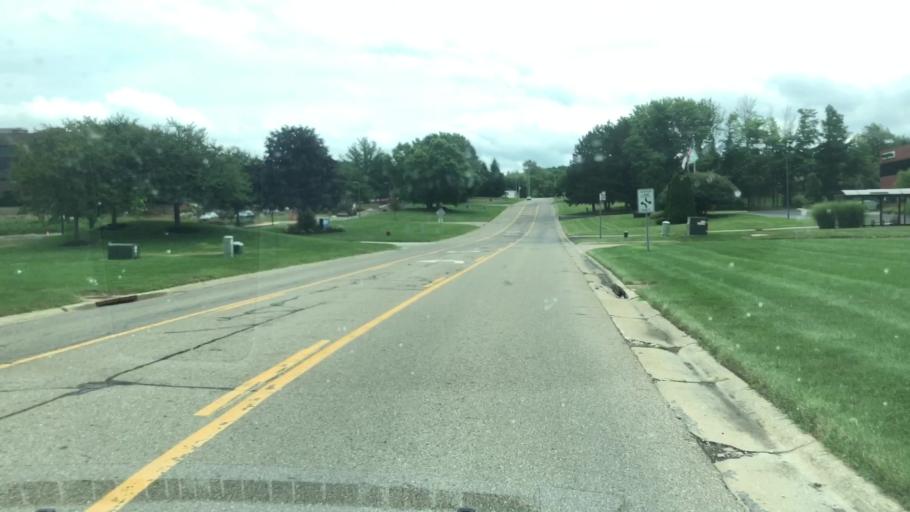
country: US
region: Ohio
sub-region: Summit County
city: Montrose-Ghent
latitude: 41.1420
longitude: -81.6422
